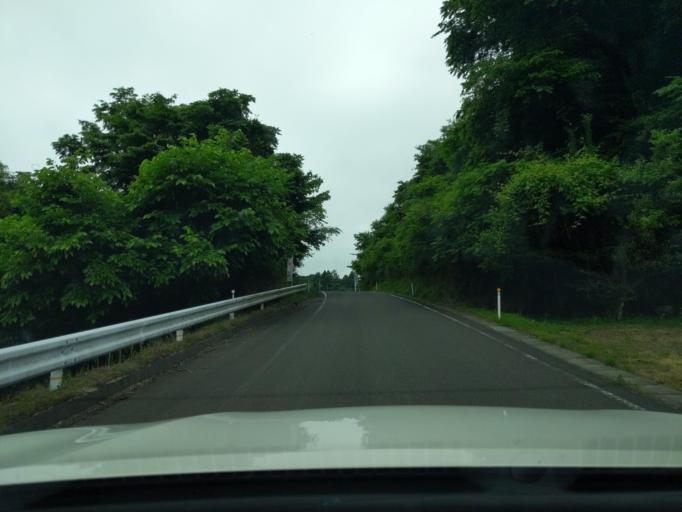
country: JP
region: Fukushima
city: Miharu
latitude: 37.4123
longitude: 140.4427
